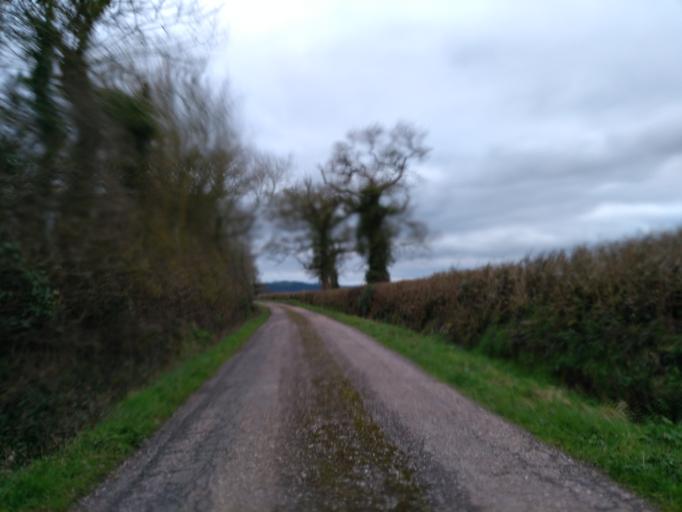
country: GB
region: England
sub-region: Devon
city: Heavitree
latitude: 50.7980
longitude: -3.4998
